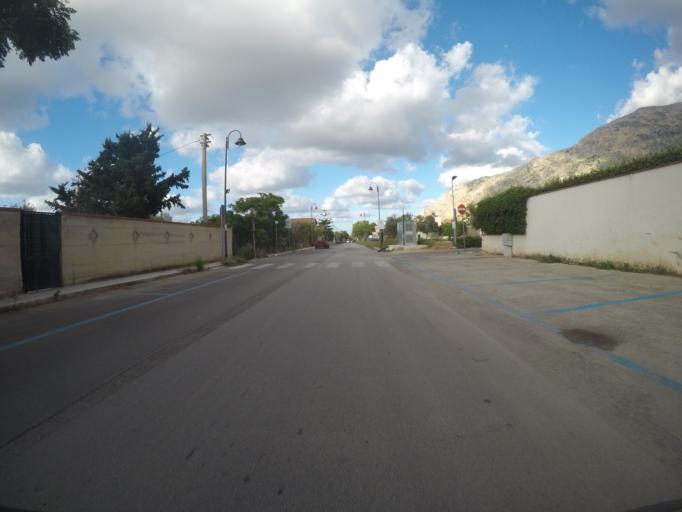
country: IT
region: Sicily
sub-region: Palermo
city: Isola delle Femmine
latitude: 38.1863
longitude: 13.2423
